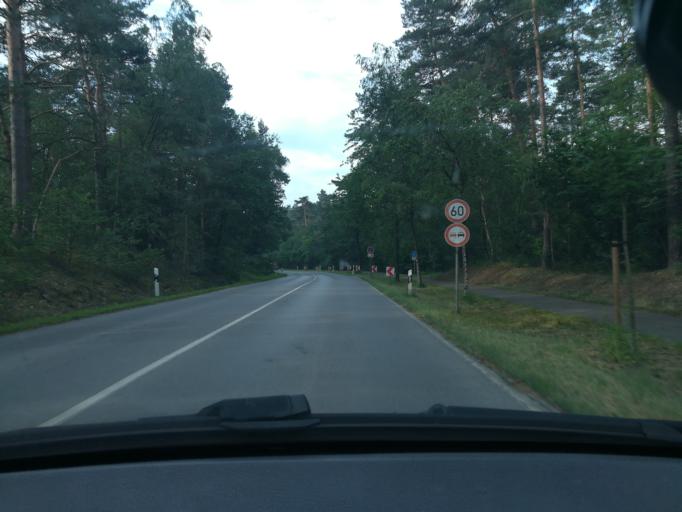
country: DE
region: North Rhine-Westphalia
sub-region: Regierungsbezirk Detmold
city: Oerlinghausen
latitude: 51.9237
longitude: 8.6555
